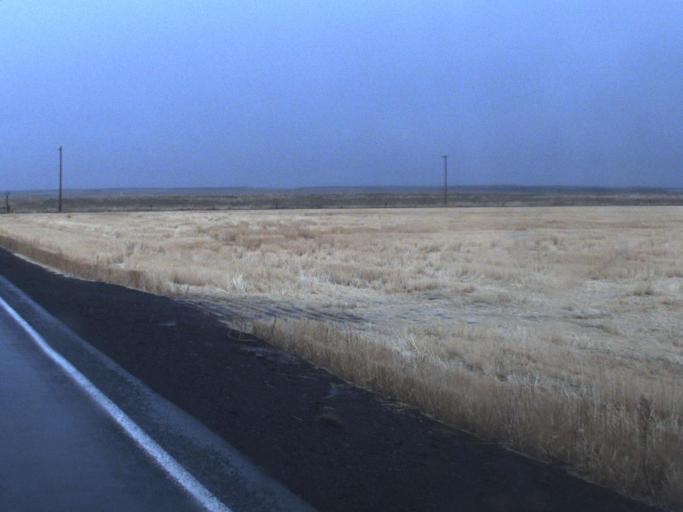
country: US
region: Washington
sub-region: Spokane County
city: Medical Lake
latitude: 47.2083
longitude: -117.8894
